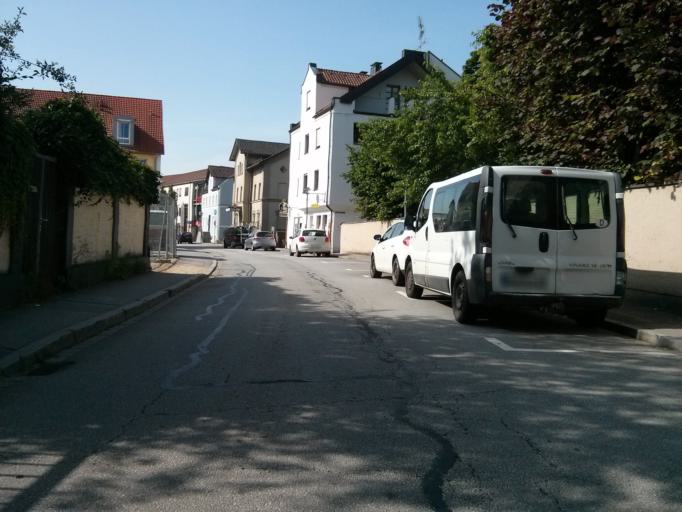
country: DE
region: Bavaria
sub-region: Lower Bavaria
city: Deggendorf
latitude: 48.8335
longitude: 12.9598
